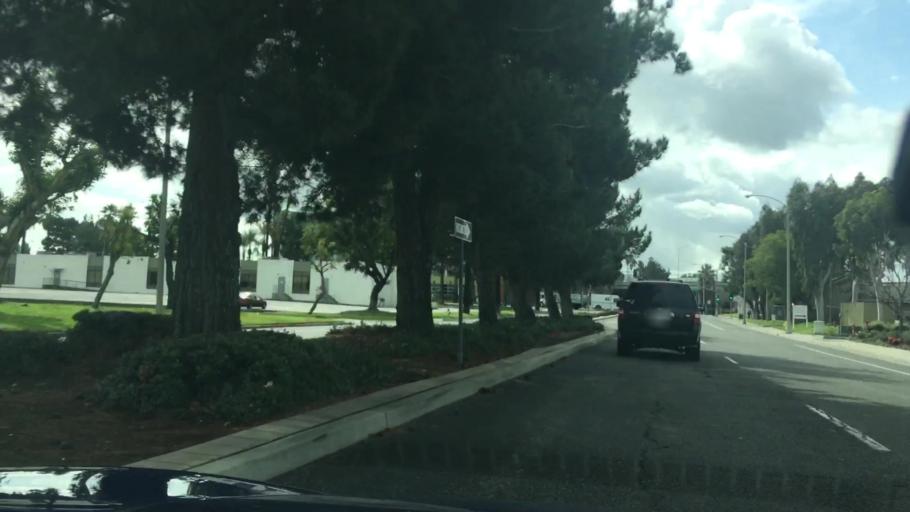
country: US
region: California
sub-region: Riverside County
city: Highgrove
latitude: 33.9918
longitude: -117.3485
